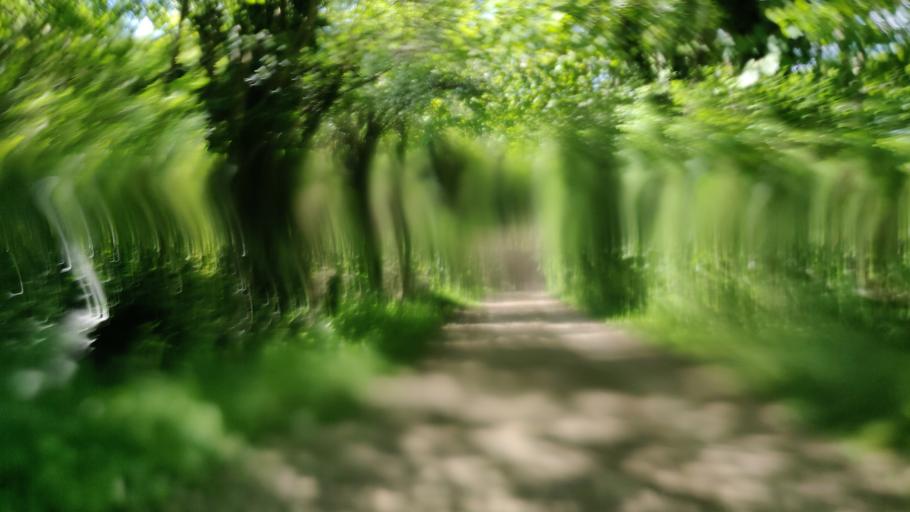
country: GB
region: England
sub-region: West Sussex
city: Rudgwick
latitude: 51.0677
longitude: -0.4134
